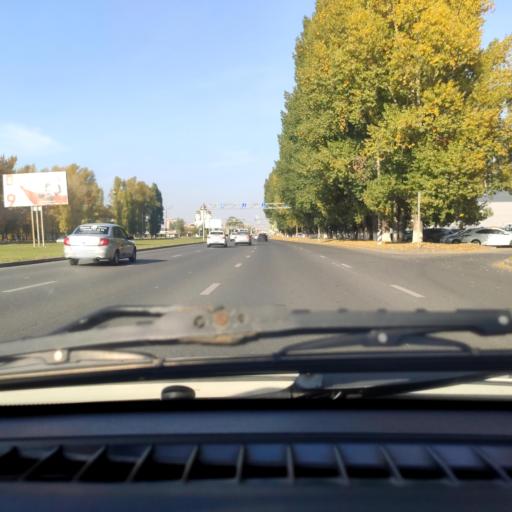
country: RU
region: Samara
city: Tol'yatti
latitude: 53.5126
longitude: 49.2780
